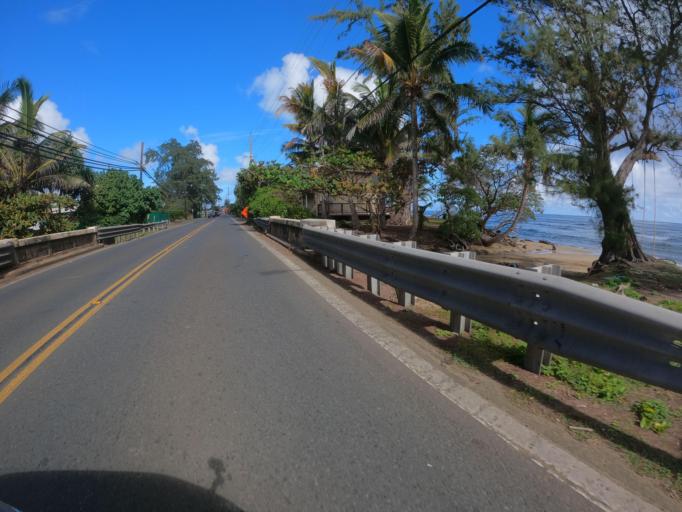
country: US
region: Hawaii
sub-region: Honolulu County
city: Hau'ula
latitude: 21.6151
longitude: -157.9134
